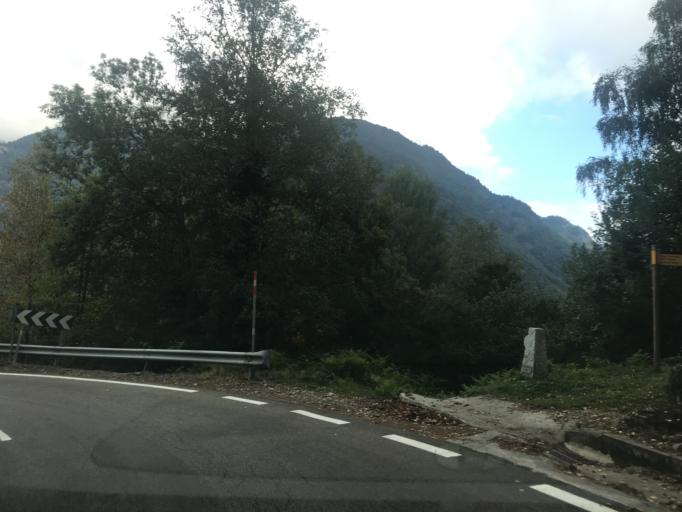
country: ES
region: Catalonia
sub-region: Provincia de Lleida
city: Les
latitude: 42.7731
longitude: 0.6807
